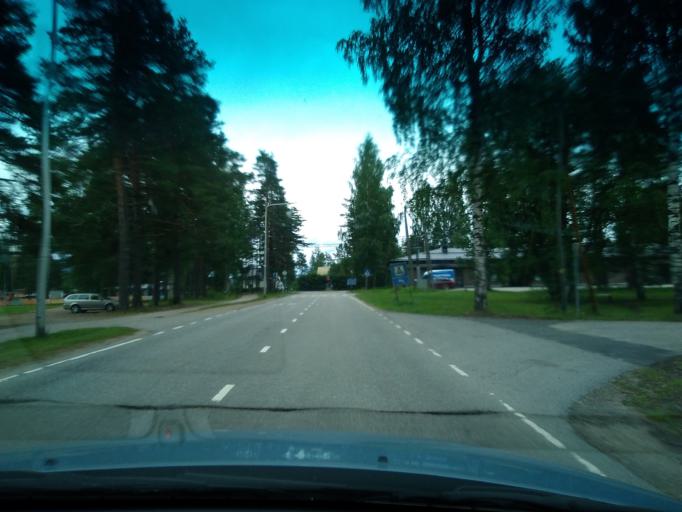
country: FI
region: Central Finland
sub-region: Keuruu
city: Multia
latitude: 62.4104
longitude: 24.7989
